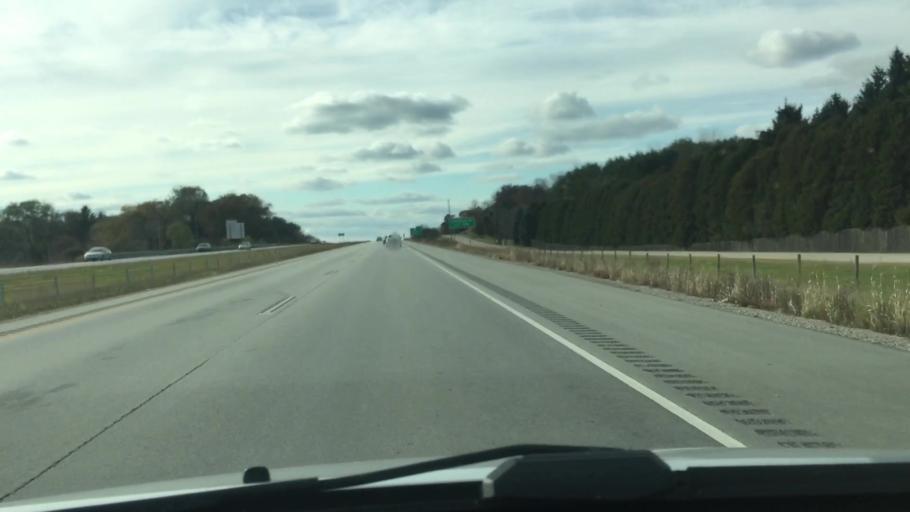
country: US
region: Wisconsin
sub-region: Waukesha County
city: Nashotah
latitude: 43.1023
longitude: -88.3895
